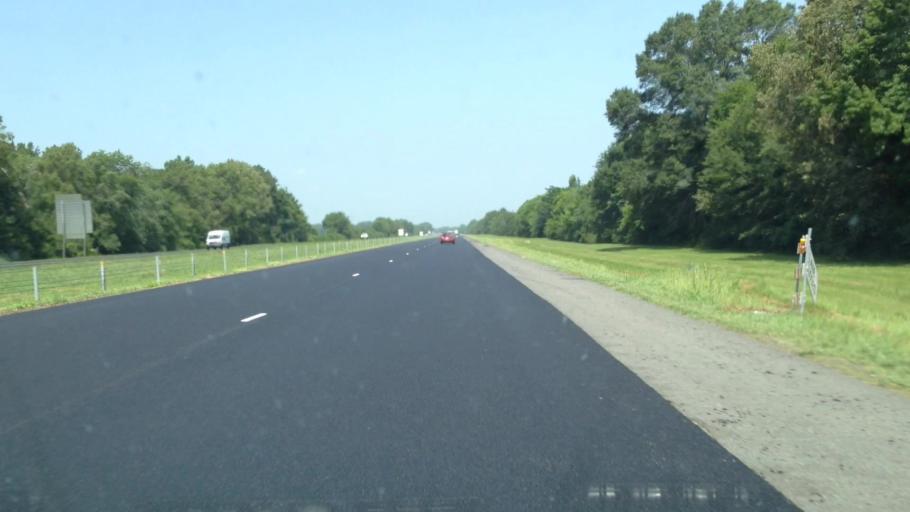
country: US
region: Louisiana
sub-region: Richland Parish
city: Rayville
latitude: 32.4603
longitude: -91.7781
